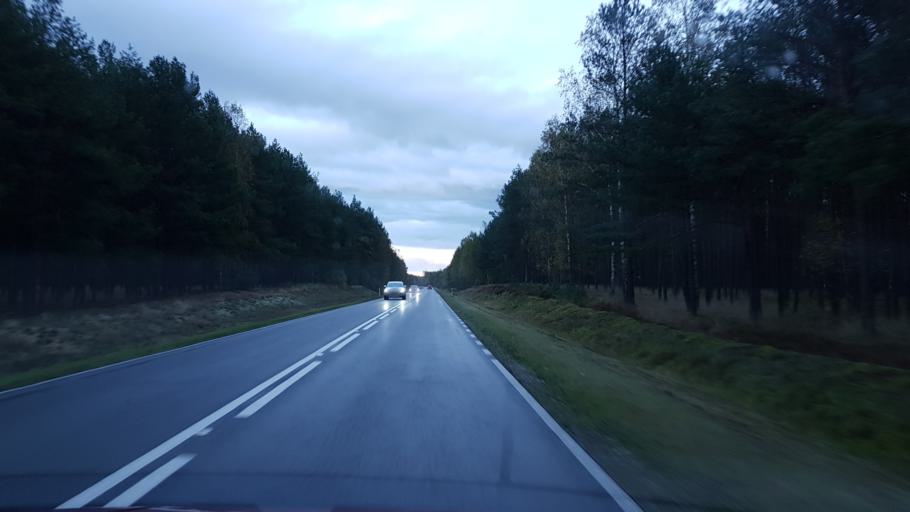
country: PL
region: Greater Poland Voivodeship
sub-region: Powiat pilski
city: Pila
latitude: 53.1984
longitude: 16.8306
